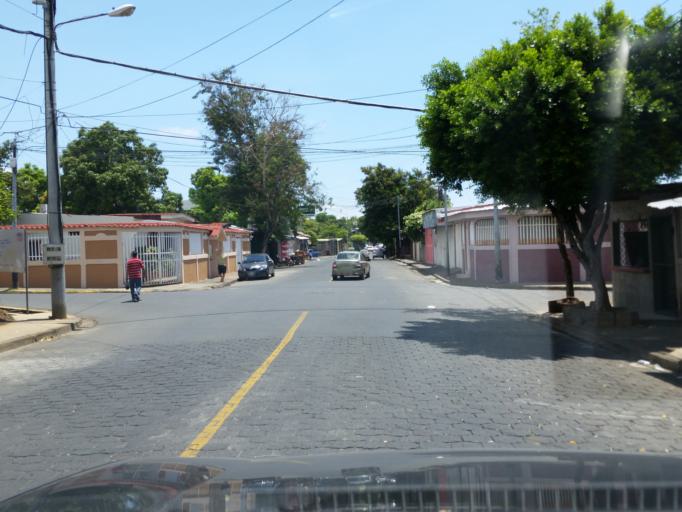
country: NI
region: Managua
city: Managua
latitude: 12.1390
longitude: -86.2522
